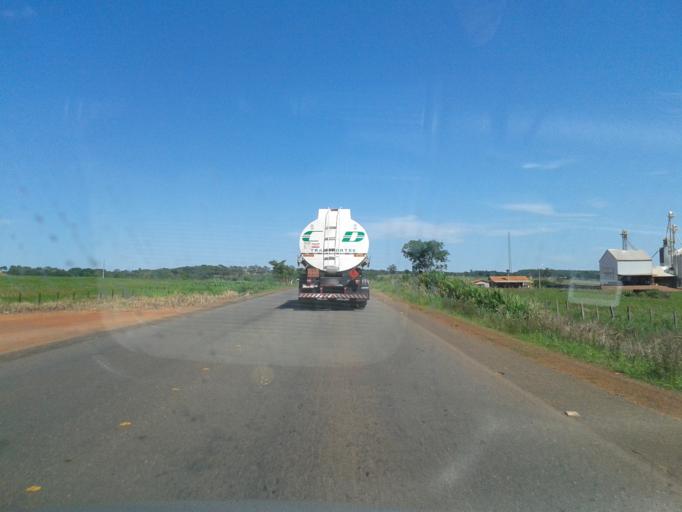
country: BR
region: Goias
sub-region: Bela Vista De Goias
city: Bela Vista de Goias
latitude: -17.0419
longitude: -48.9433
